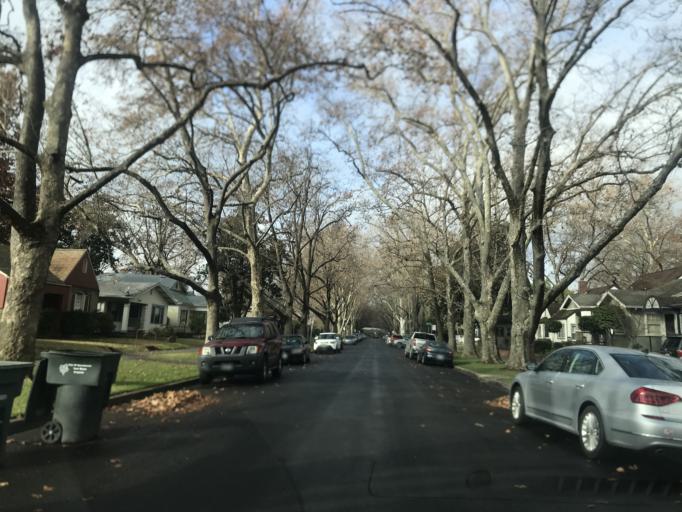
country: US
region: California
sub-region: Sacramento County
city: Sacramento
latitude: 38.5786
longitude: -121.4597
